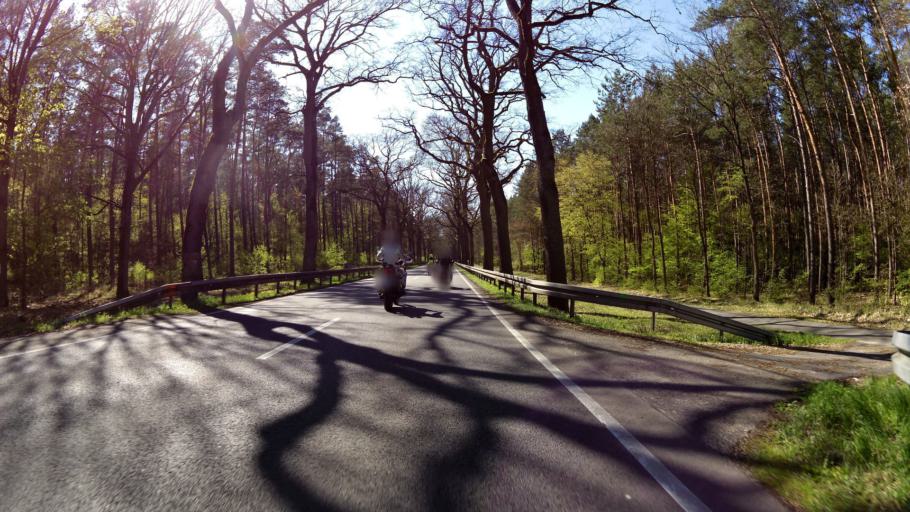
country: DE
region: Brandenburg
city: Waldsieversdorf
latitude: 52.4979
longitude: 14.0746
